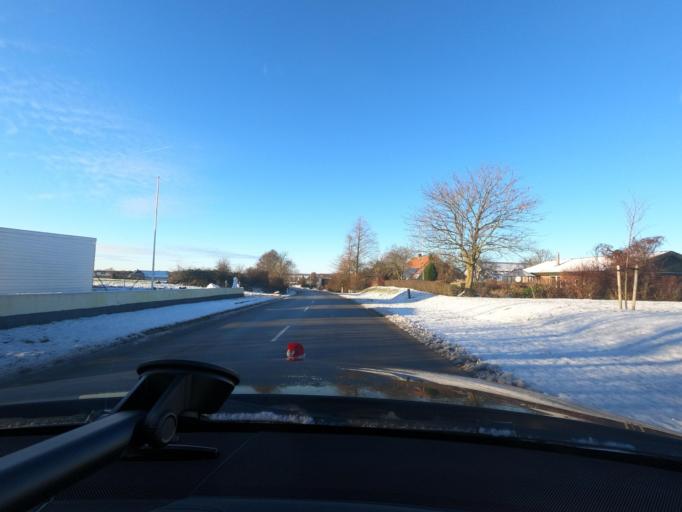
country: DK
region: South Denmark
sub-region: Sonderborg Kommune
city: Horuphav
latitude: 54.8760
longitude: 9.9239
